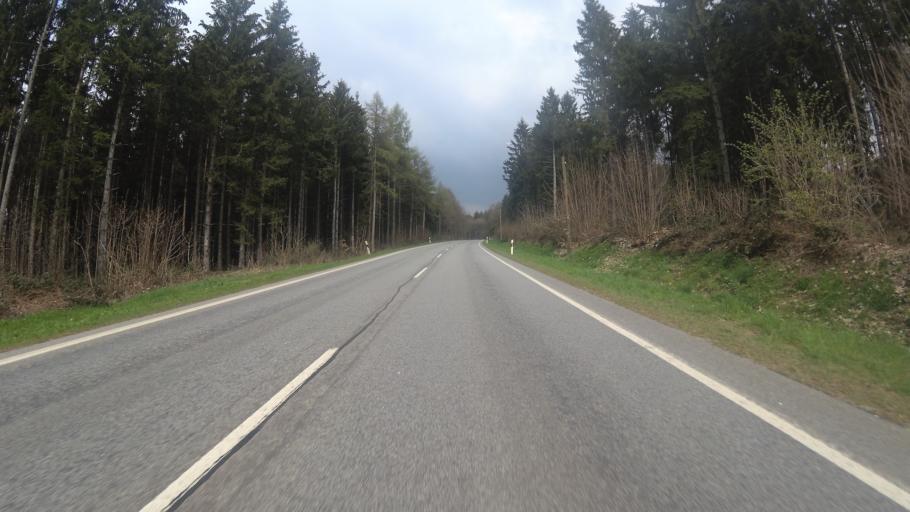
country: DE
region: Saarland
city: Nonnweiler
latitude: 49.6200
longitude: 6.9627
